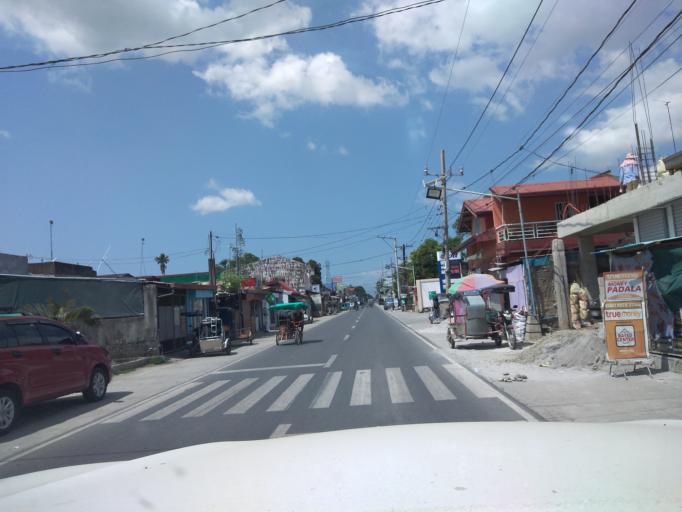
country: PH
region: Central Luzon
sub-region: Province of Pampanga
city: Bahay Pare
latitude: 15.0277
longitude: 120.8824
